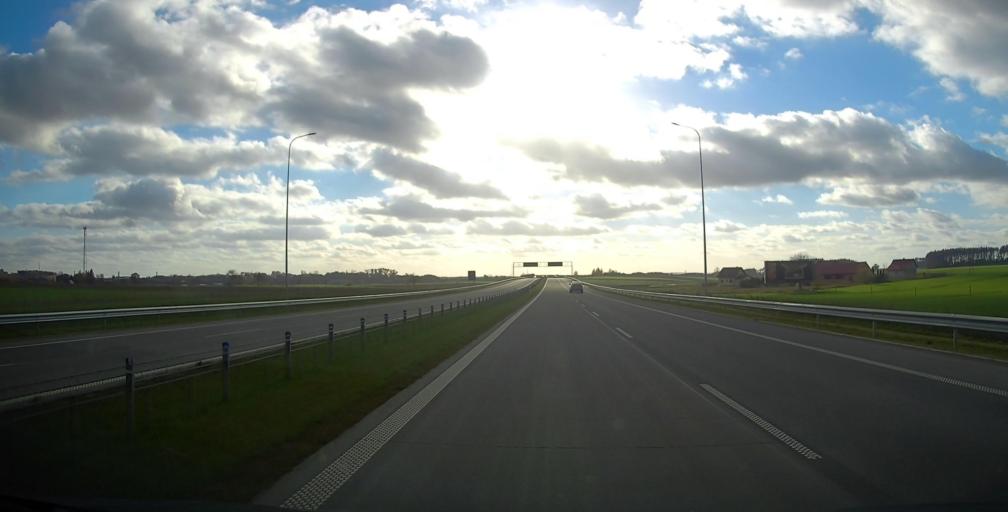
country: PL
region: Podlasie
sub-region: Powiat lomzynski
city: Piatnica
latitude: 53.2640
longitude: 22.1197
